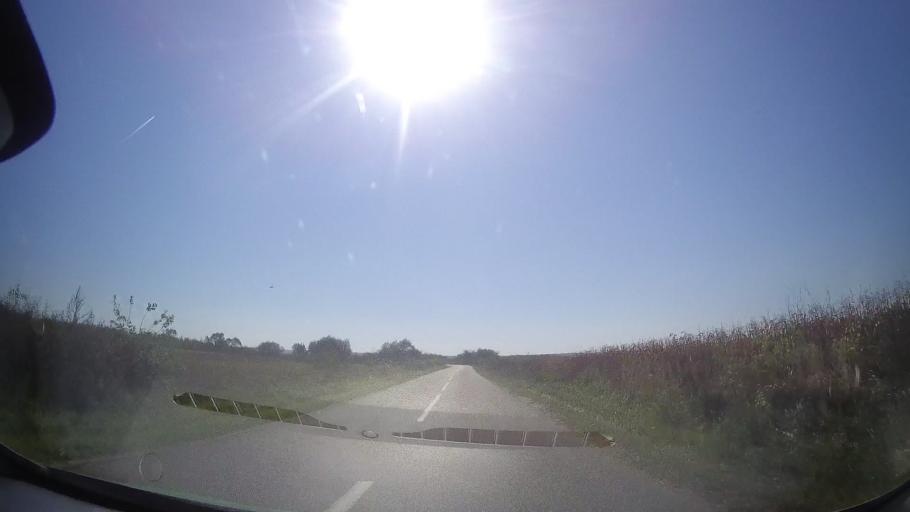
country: RO
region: Timis
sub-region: Comuna Bethausen
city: Bethausen
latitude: 45.8234
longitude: 21.9597
